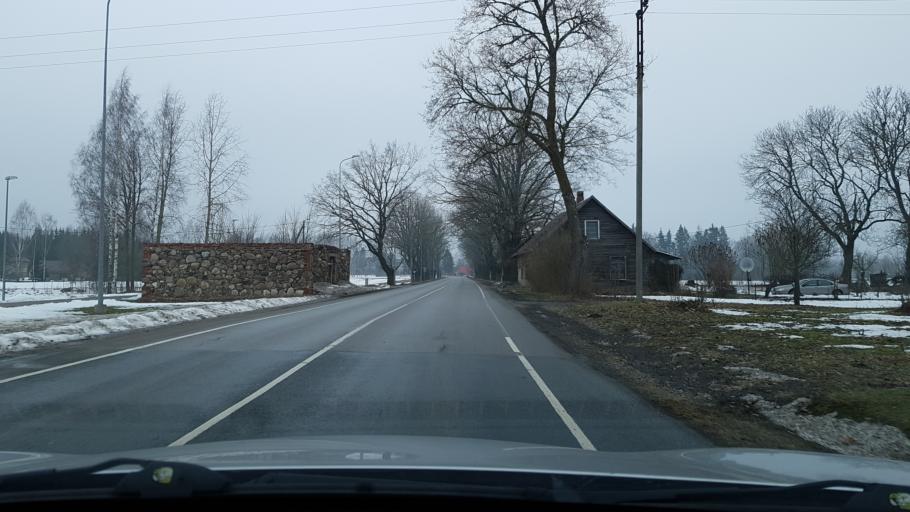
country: EE
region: Valgamaa
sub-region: Torva linn
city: Torva
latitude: 58.2305
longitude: 25.8825
